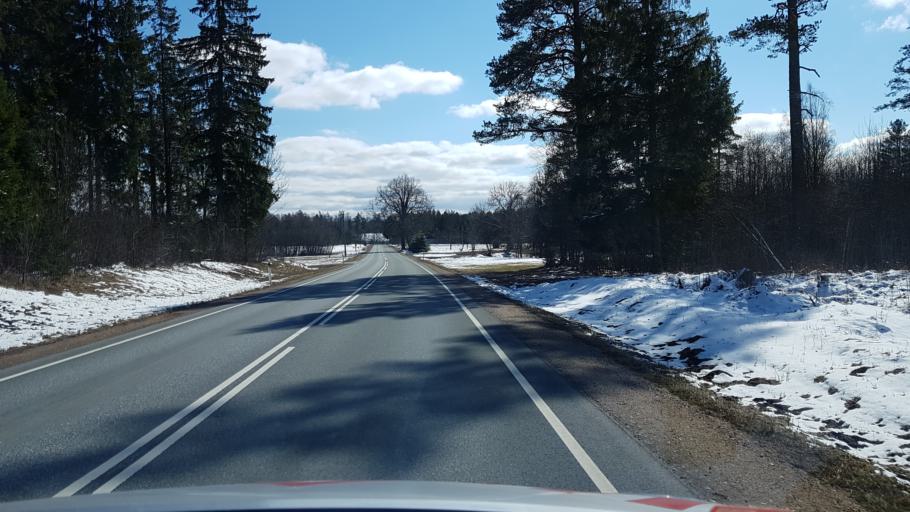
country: EE
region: Laeaene-Virumaa
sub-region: Tapa vald
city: Tapa
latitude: 59.4177
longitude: 25.9940
